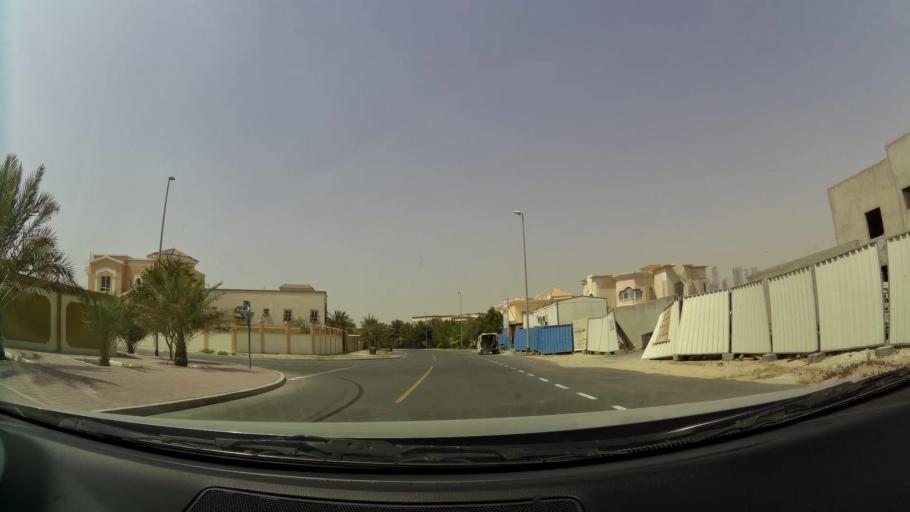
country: AE
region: Ash Shariqah
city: Sharjah
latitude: 25.2459
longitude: 55.4295
